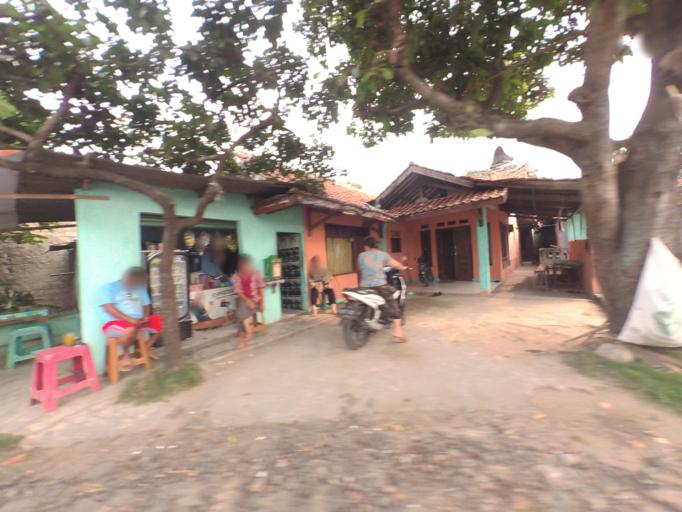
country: ID
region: West Java
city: Ciampea
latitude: -6.5645
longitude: 106.6763
